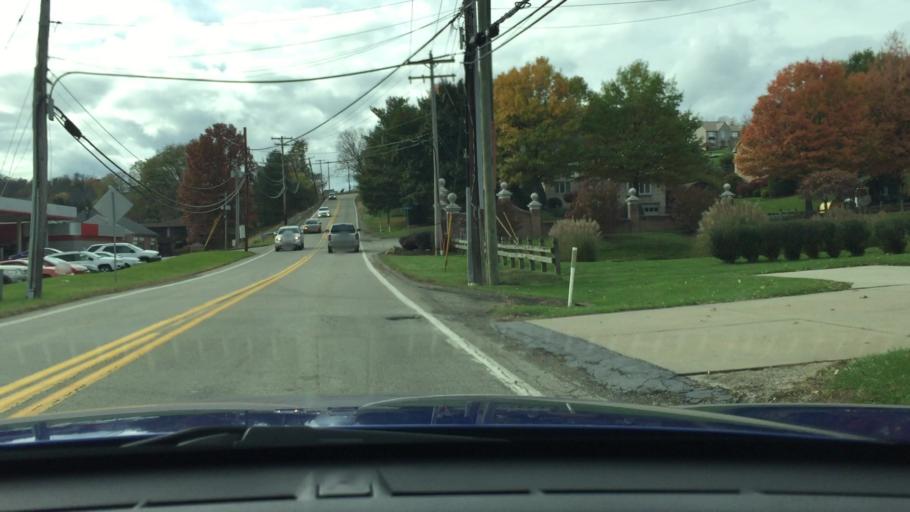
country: US
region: Pennsylvania
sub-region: Washington County
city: Canonsburg
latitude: 40.2565
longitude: -80.1530
